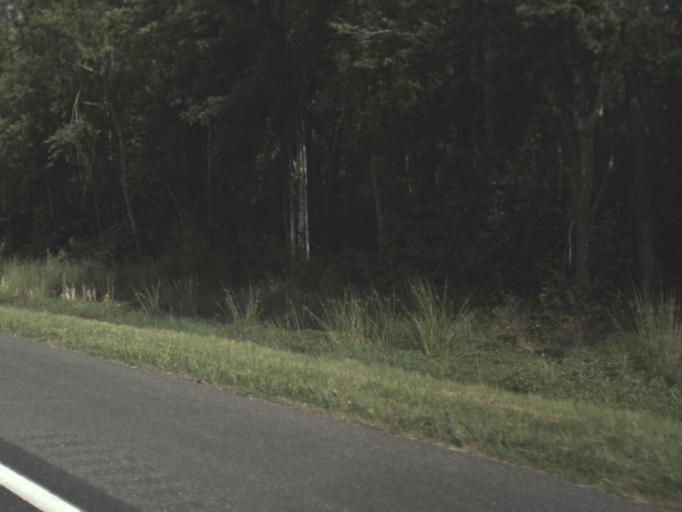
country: US
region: Florida
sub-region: Baker County
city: Macclenny
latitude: 30.2538
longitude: -82.2015
